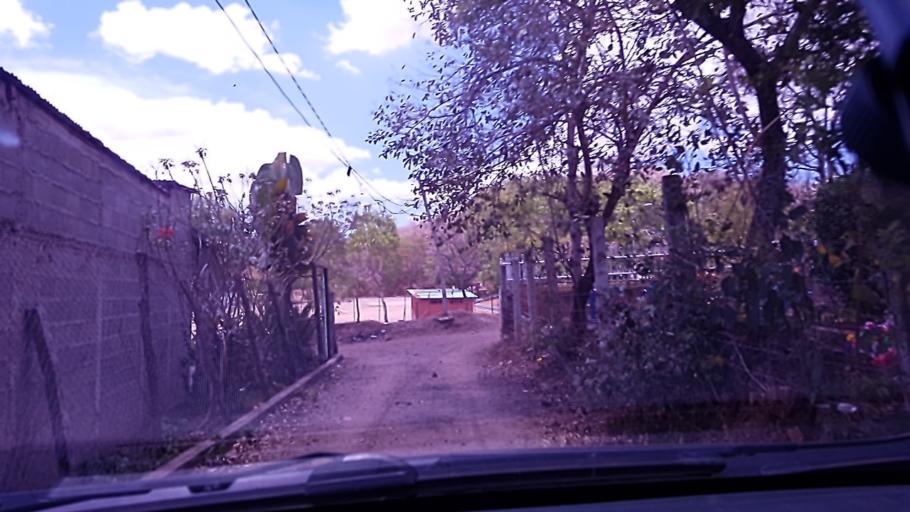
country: NI
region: Esteli
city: Condega
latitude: 13.3596
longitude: -86.4006
